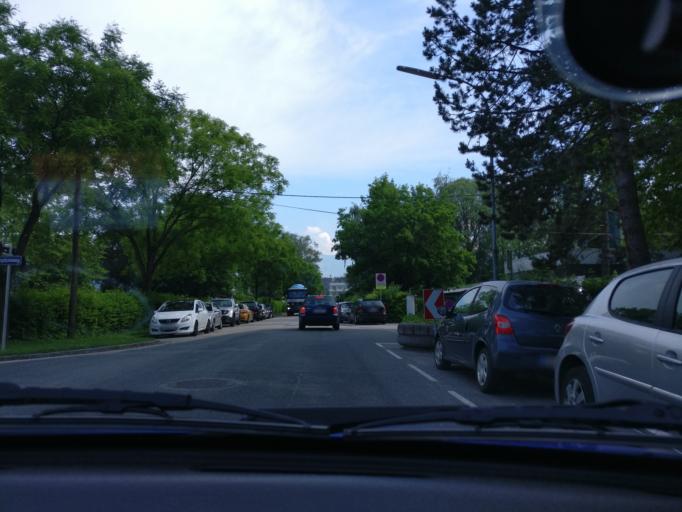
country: AT
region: Carinthia
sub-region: Klagenfurt am Woerthersee
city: Klagenfurt am Woerthersee
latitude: 46.6164
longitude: 14.2677
